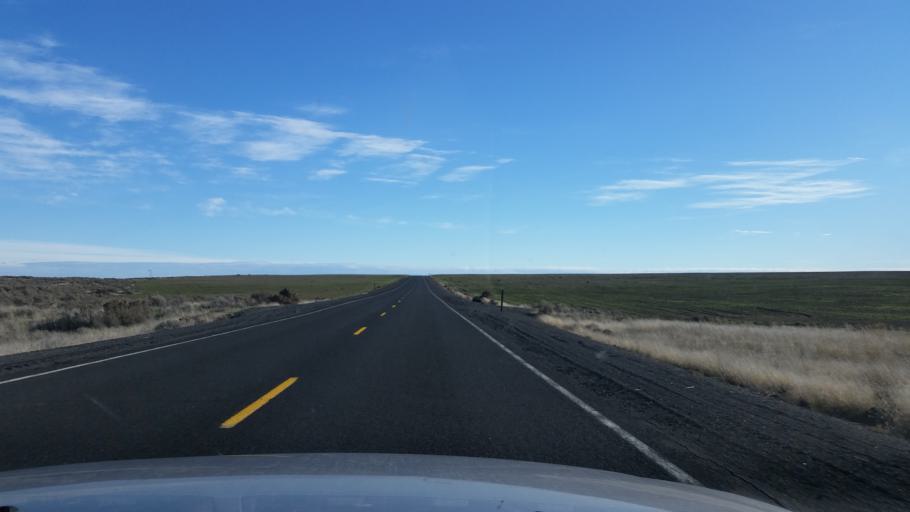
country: US
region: Washington
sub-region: Grant County
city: Warden
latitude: 47.3548
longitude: -118.9480
